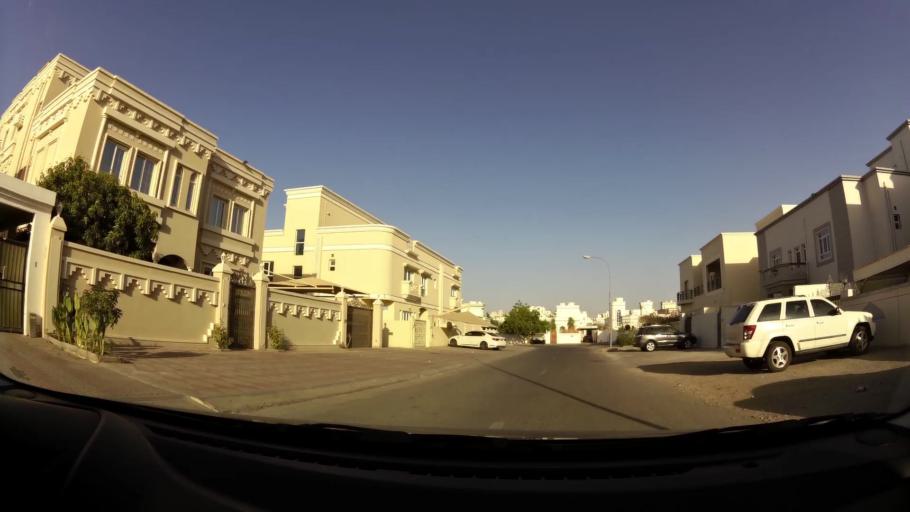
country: OM
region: Muhafazat Masqat
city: As Sib al Jadidah
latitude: 23.6088
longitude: 58.2213
